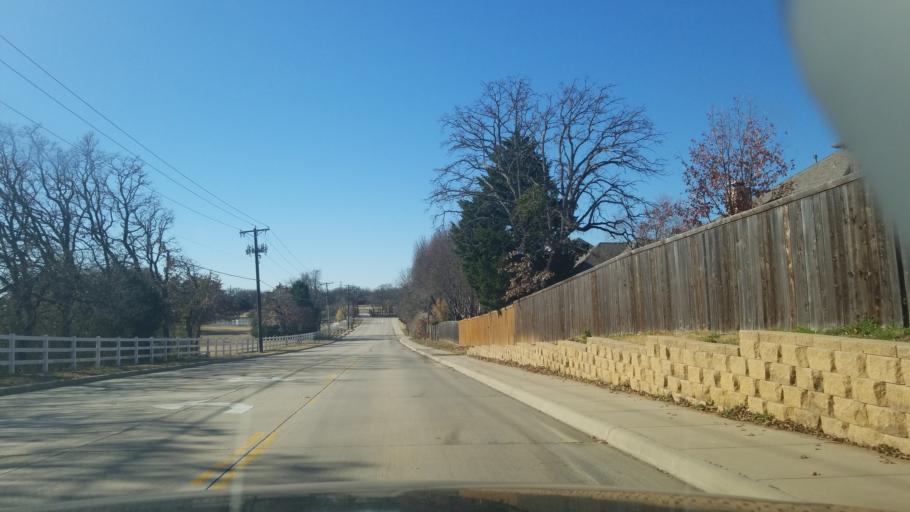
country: US
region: Texas
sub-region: Denton County
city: Corinth
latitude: 33.1542
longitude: -97.0758
